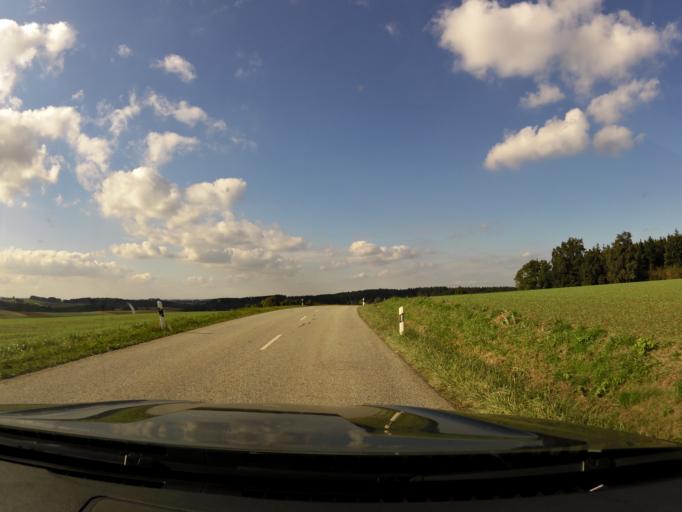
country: DE
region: Bavaria
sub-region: Lower Bavaria
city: Kumhausen
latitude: 48.4802
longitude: 12.1417
